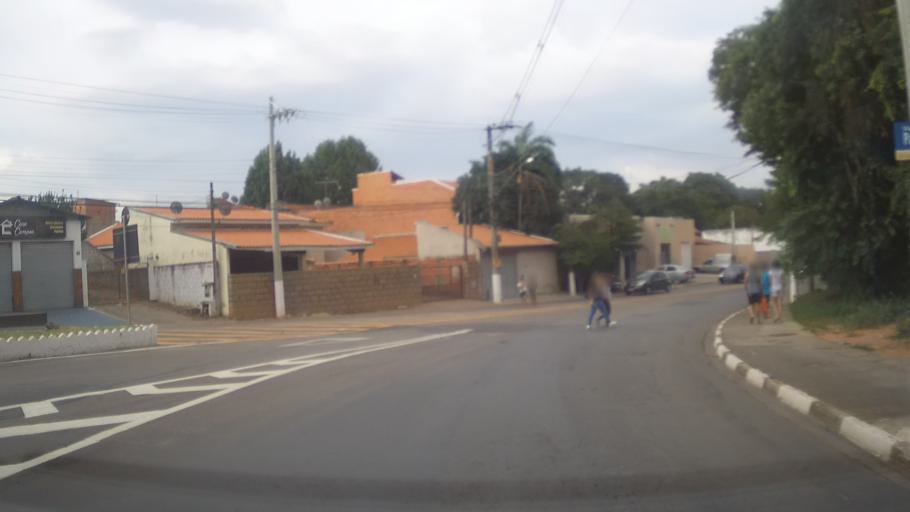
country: BR
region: Sao Paulo
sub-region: Itupeva
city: Itupeva
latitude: -23.1739
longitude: -47.0524
